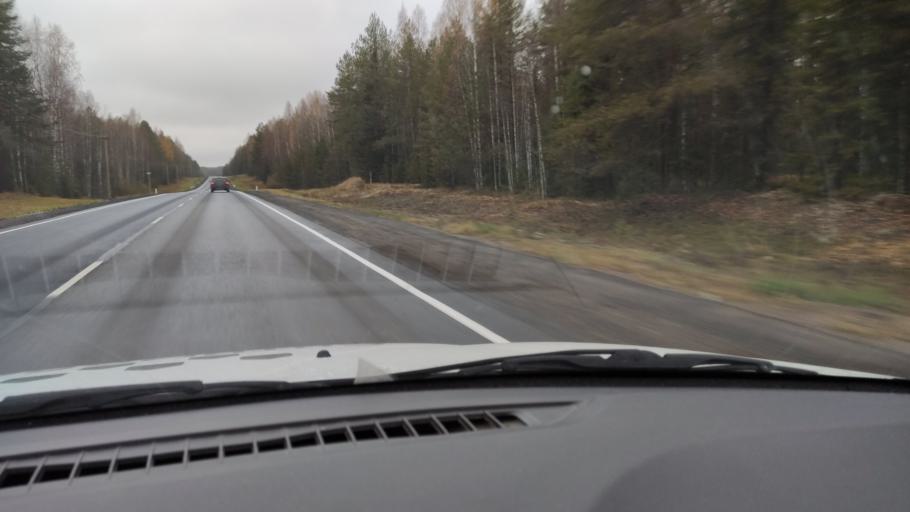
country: RU
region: Kirov
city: Belaya Kholunitsa
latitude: 58.9155
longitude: 51.1510
